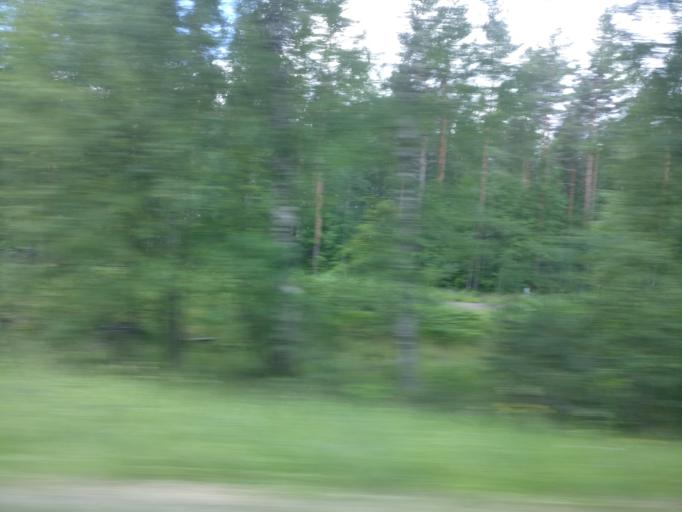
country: FI
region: Paijanne Tavastia
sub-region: Lahti
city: Hartola
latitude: 61.6487
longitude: 26.0287
